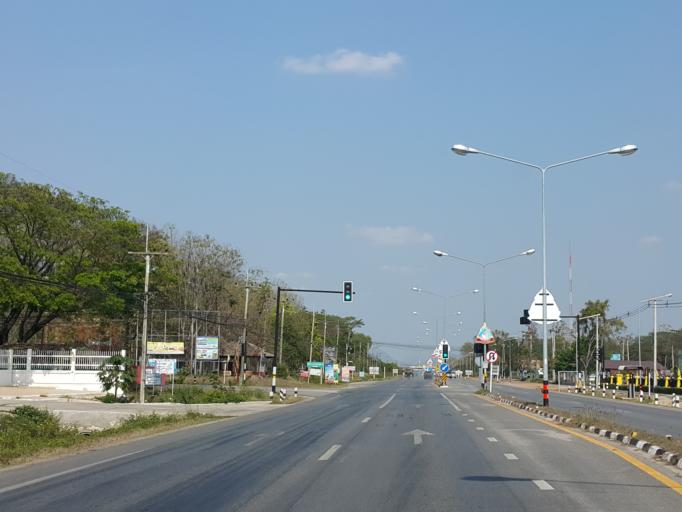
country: TH
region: Lampang
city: Mae Mo
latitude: 18.2735
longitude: 99.6499
